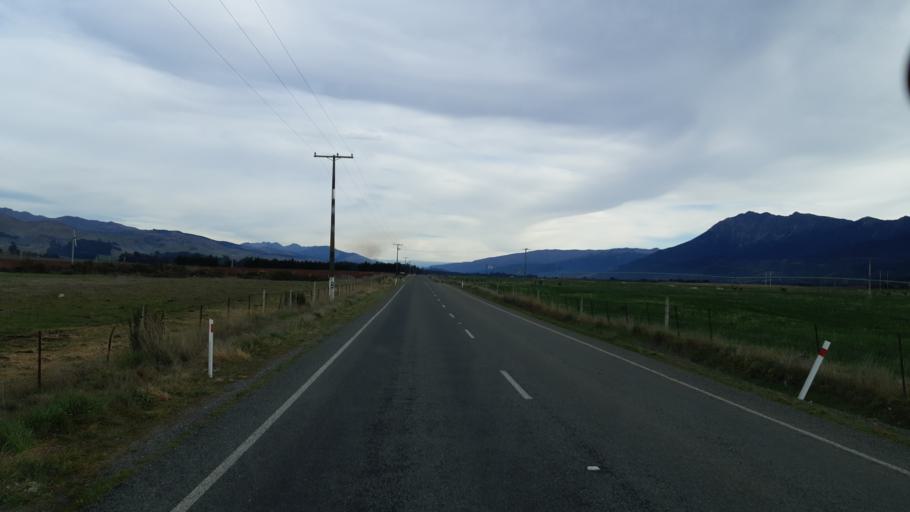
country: NZ
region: Tasman
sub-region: Tasman District
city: Richmond
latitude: -41.6121
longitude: 173.3914
